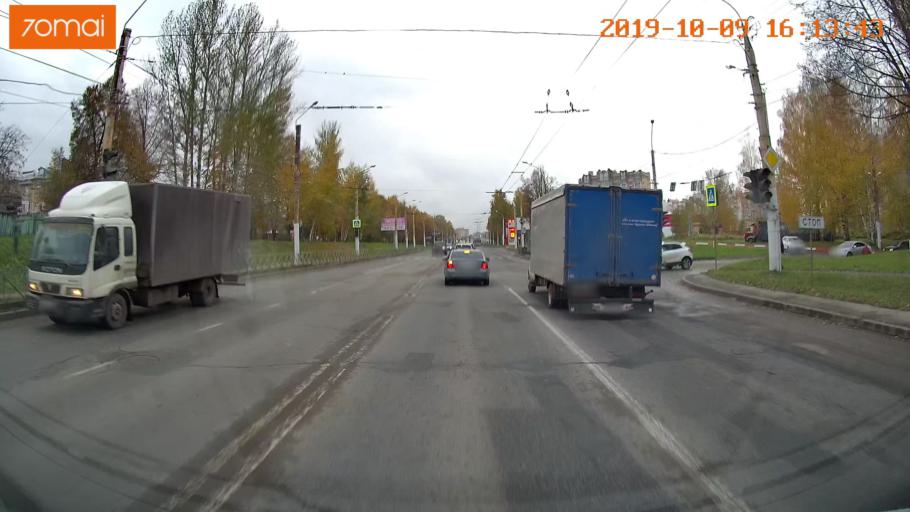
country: RU
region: Kostroma
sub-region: Kostromskoy Rayon
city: Kostroma
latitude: 57.7454
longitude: 40.9275
